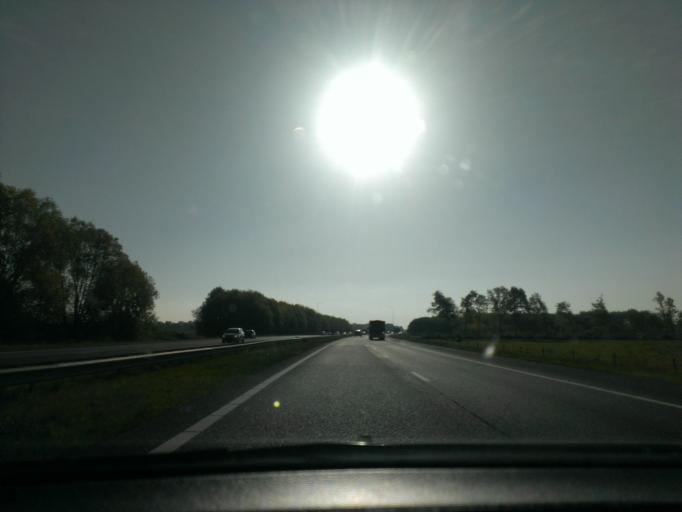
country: NL
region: Drenthe
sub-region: Gemeente Meppel
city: Meppel
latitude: 52.6858
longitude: 6.2394
